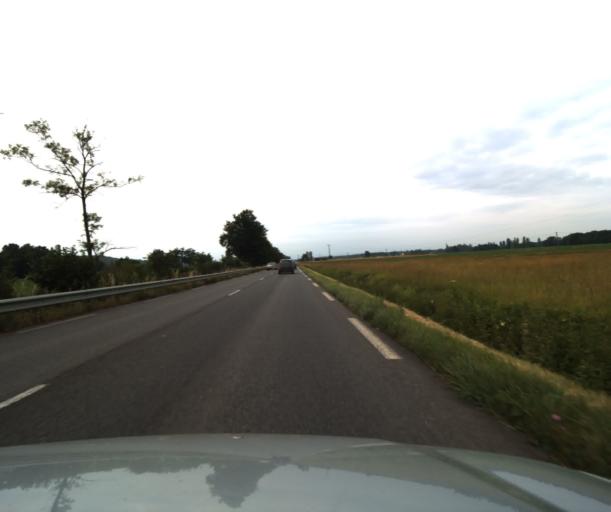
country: FR
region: Midi-Pyrenees
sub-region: Departement des Hautes-Pyrenees
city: Rabastens-de-Bigorre
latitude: 43.3621
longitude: 0.1411
